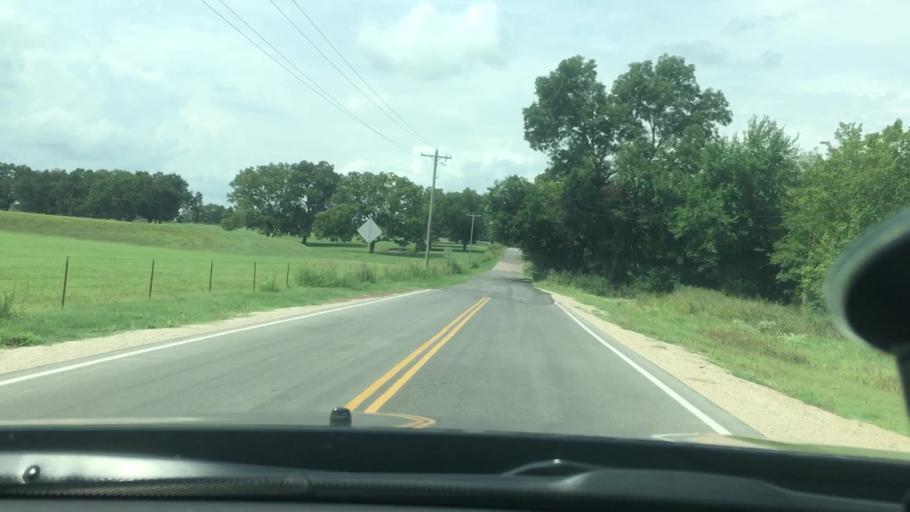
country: US
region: Oklahoma
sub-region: Carter County
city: Dickson
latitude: 34.2308
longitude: -96.9111
